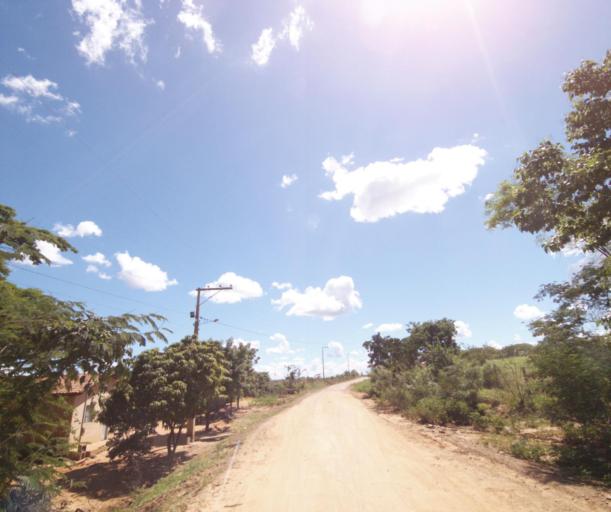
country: BR
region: Bahia
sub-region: Carinhanha
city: Carinhanha
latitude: -14.2162
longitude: -44.2858
